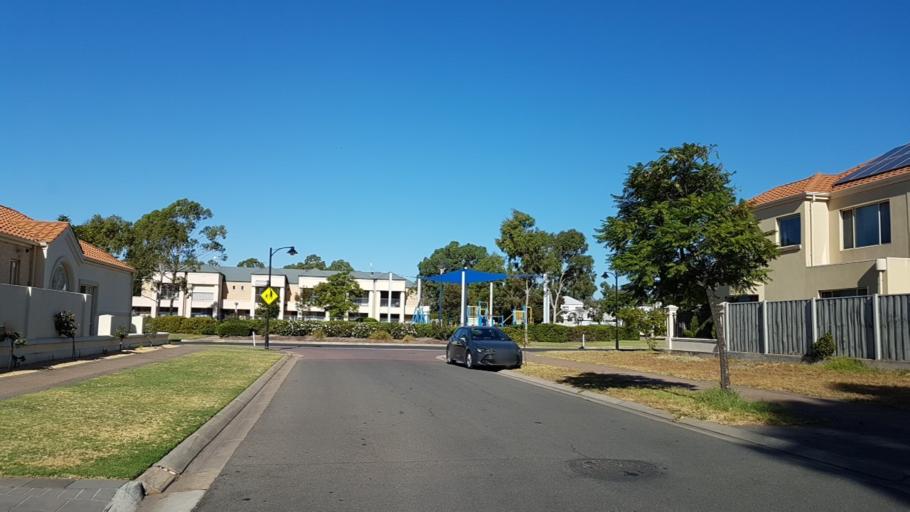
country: AU
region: South Australia
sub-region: Salisbury
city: Ingle Farm
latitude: -34.8131
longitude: 138.6101
